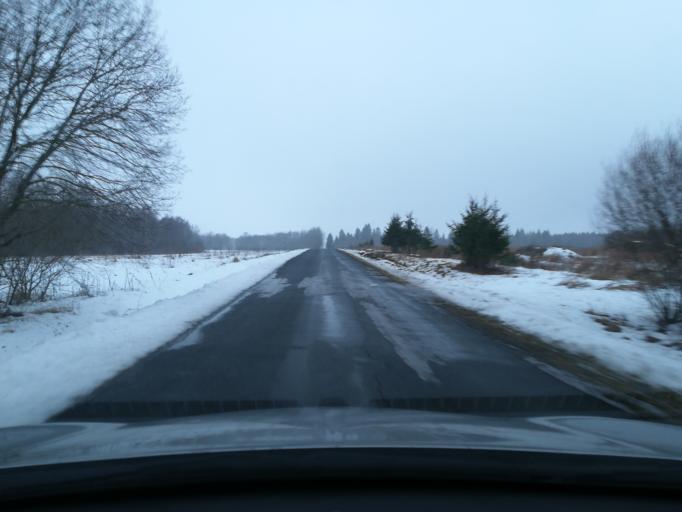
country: EE
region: Harju
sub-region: Raasiku vald
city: Raasiku
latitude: 59.3441
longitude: 25.2219
